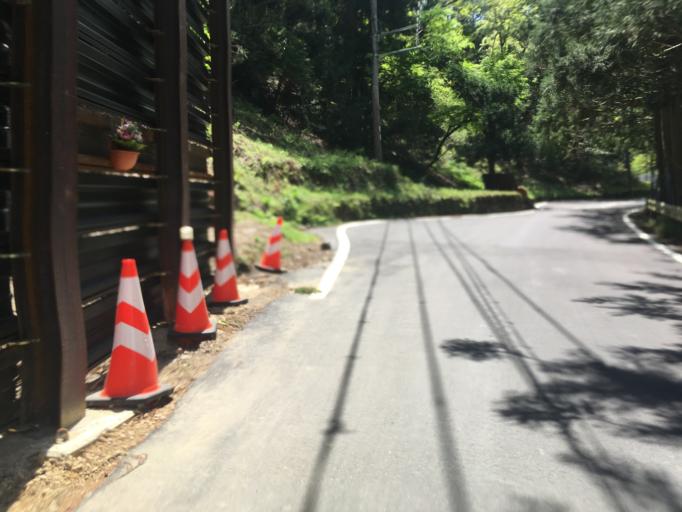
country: JP
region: Kyoto
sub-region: Kyoto-shi
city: Kamigyo-ku
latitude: 35.0937
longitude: 135.7421
